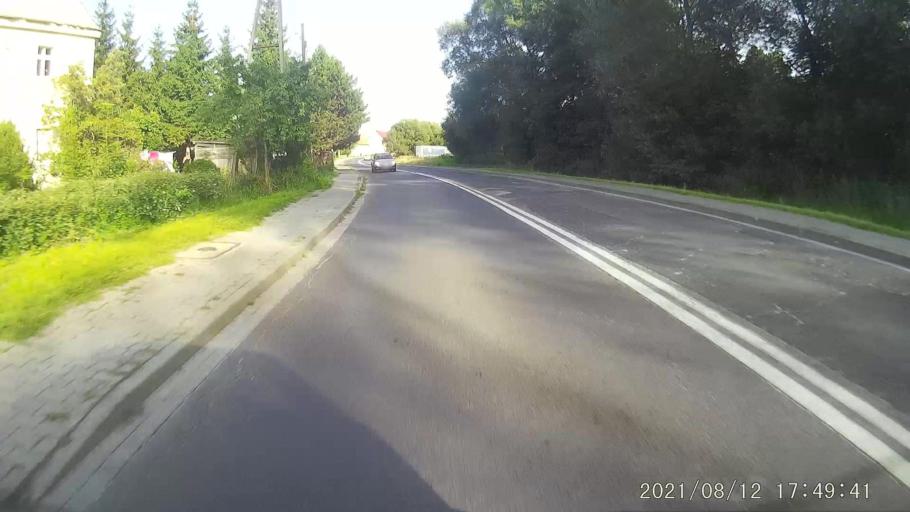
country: PL
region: Lower Silesian Voivodeship
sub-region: Powiat klodzki
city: Klodzko
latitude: 50.3615
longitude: 16.7163
